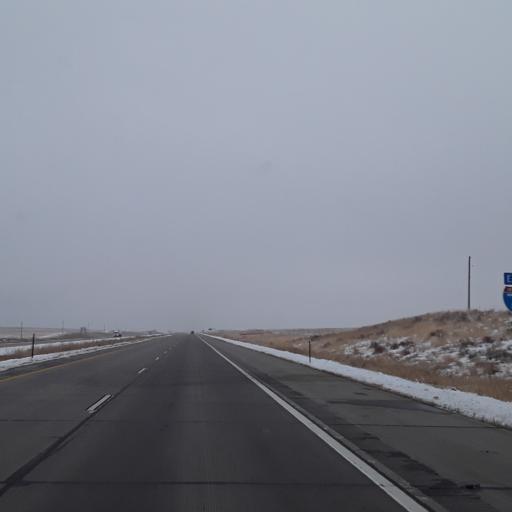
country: US
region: Colorado
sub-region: Logan County
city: Sterling
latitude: 40.5068
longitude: -103.2544
